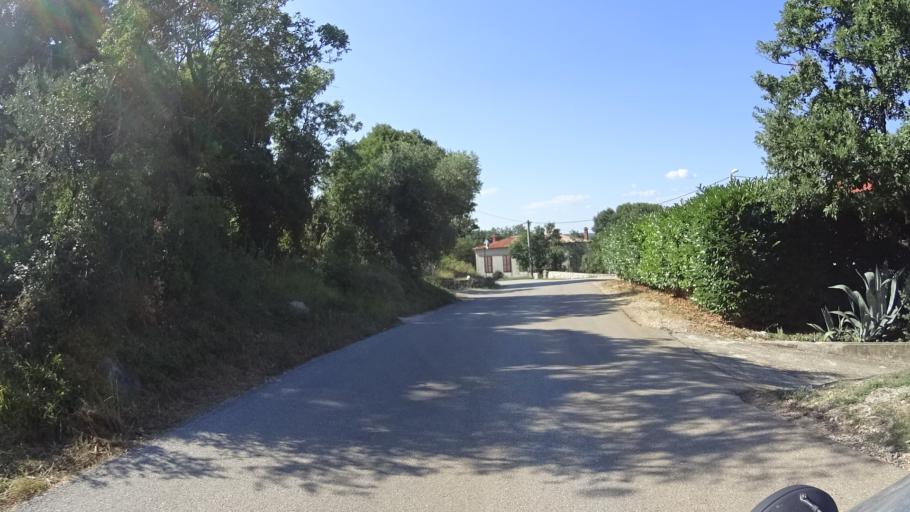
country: HR
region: Istarska
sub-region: Grad Labin
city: Rabac
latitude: 45.0104
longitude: 14.1580
